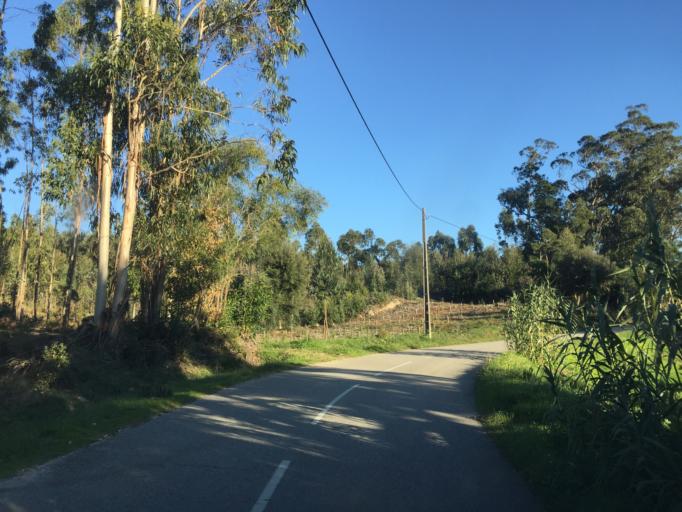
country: PT
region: Coimbra
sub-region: Figueira da Foz
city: Alhadas
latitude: 40.1625
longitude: -8.8076
